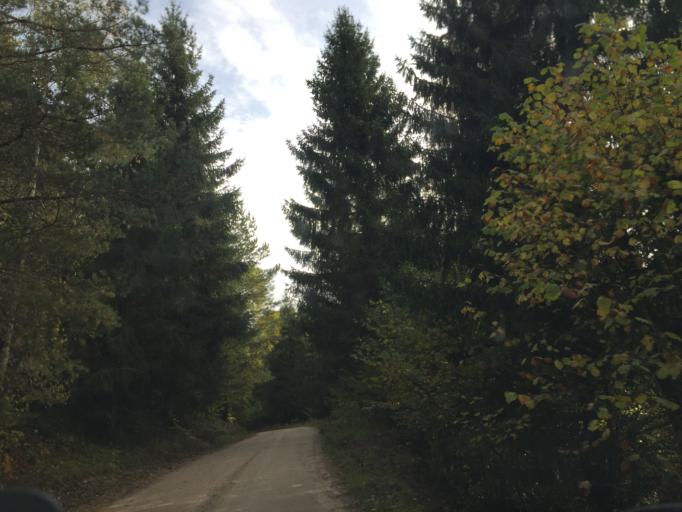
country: LV
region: Jaunpils
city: Jaunpils
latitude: 56.5851
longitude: 23.0125
